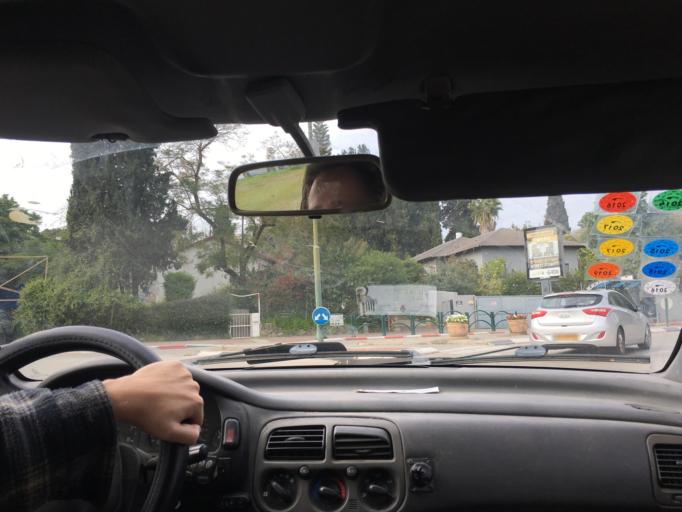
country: IL
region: Tel Aviv
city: Ramat HaSharon
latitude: 32.1348
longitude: 34.8458
